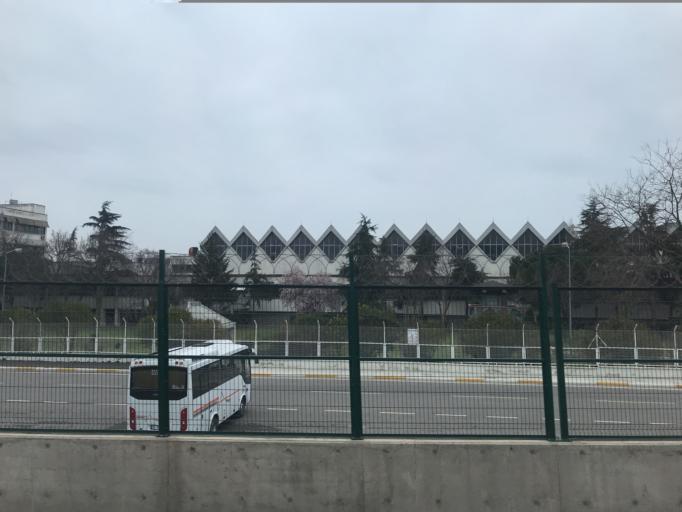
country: TR
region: Istanbul
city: Pendik
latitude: 40.8644
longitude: 29.2694
